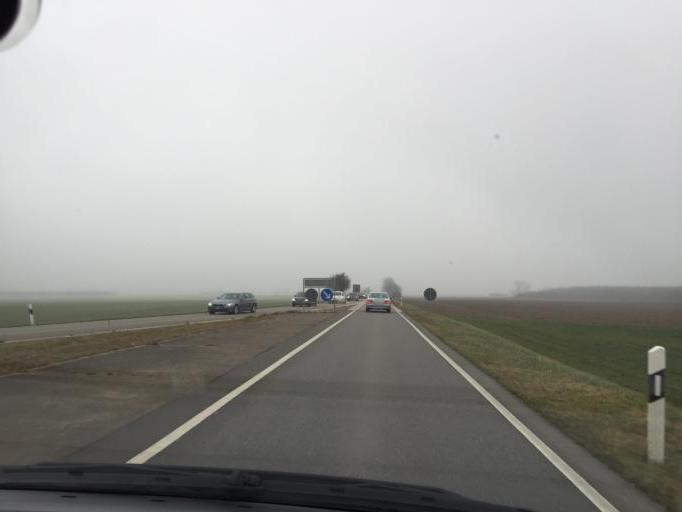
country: DE
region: Baden-Wuerttemberg
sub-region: Freiburg Region
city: Hartheim
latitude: 47.9794
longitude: 7.6467
